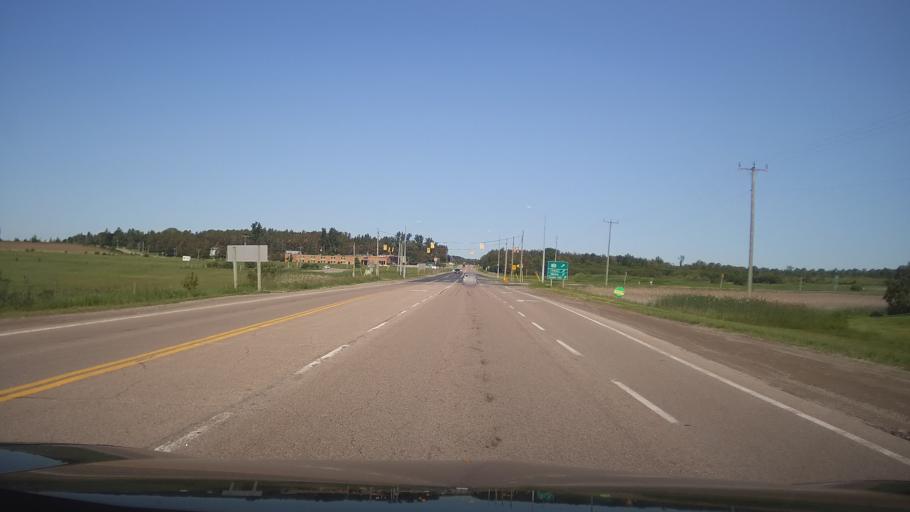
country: CA
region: Ontario
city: Omemee
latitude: 44.3455
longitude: -78.7728
